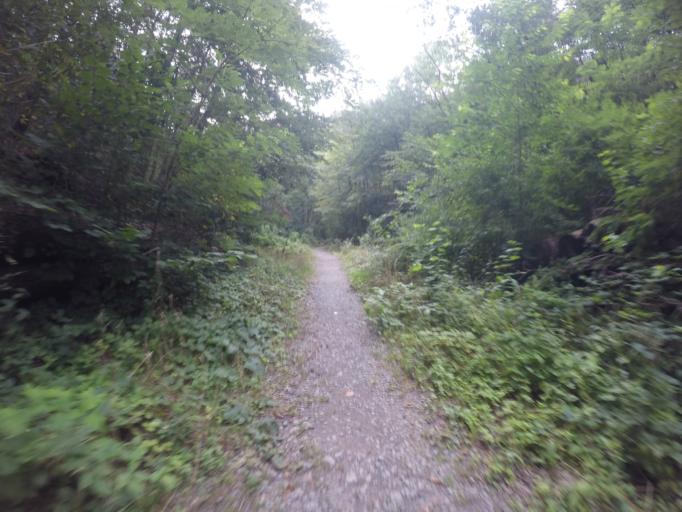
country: DE
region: Baden-Wuerttemberg
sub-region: Regierungsbezirk Stuttgart
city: Stuttgart
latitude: 48.7536
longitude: 9.1467
